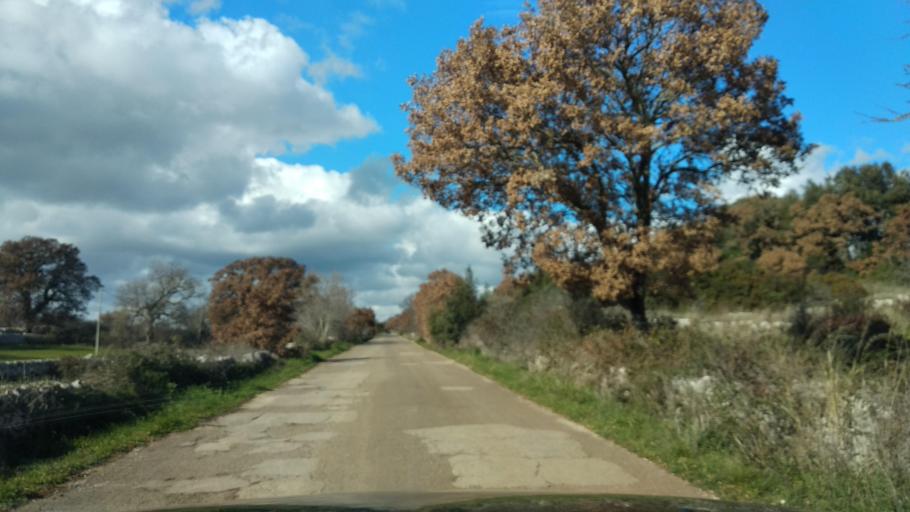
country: IT
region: Apulia
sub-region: Provincia di Brindisi
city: Casalini
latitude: 40.7175
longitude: 17.4508
